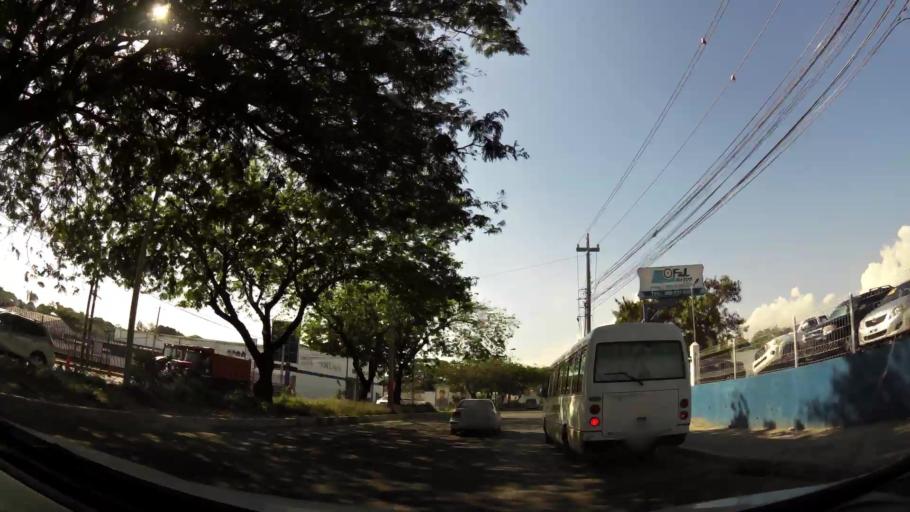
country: DO
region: San Cristobal
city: El Carril
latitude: 18.4612
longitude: -69.9921
